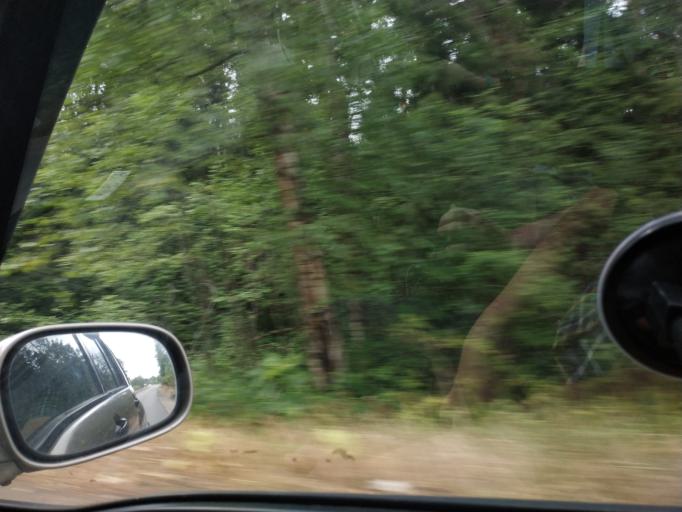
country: RU
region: Moskovskaya
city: Krasnoarmeysk
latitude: 56.0698
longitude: 38.2561
